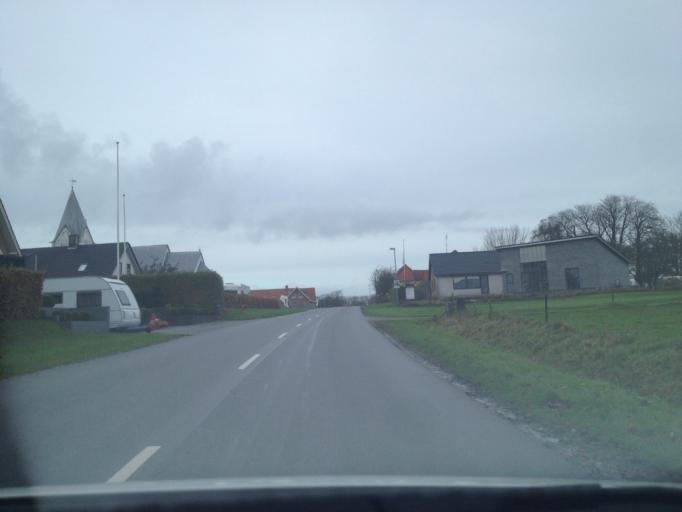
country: DK
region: South Denmark
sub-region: Esbjerg Kommune
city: Ribe
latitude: 55.2439
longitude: 8.8291
